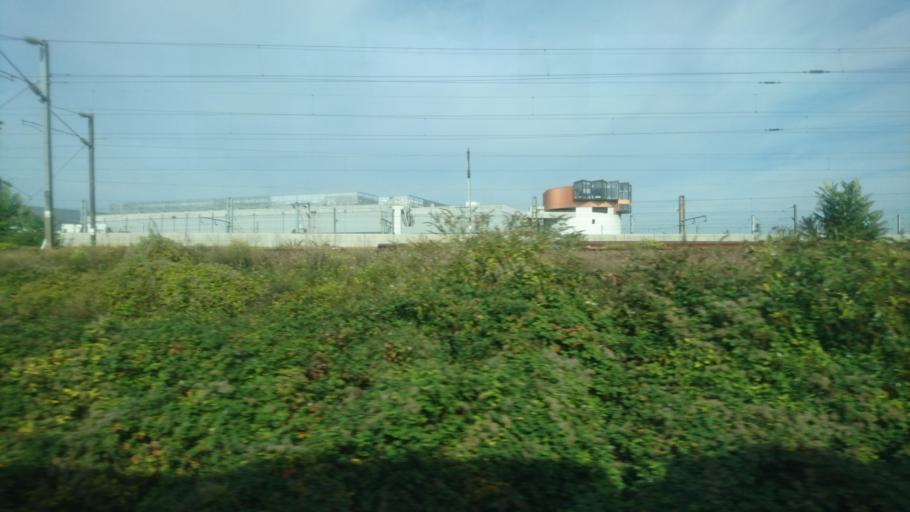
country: FR
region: Ile-de-France
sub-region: Departement de Seine-Saint-Denis
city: Pantin
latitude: 48.8985
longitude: 2.4230
